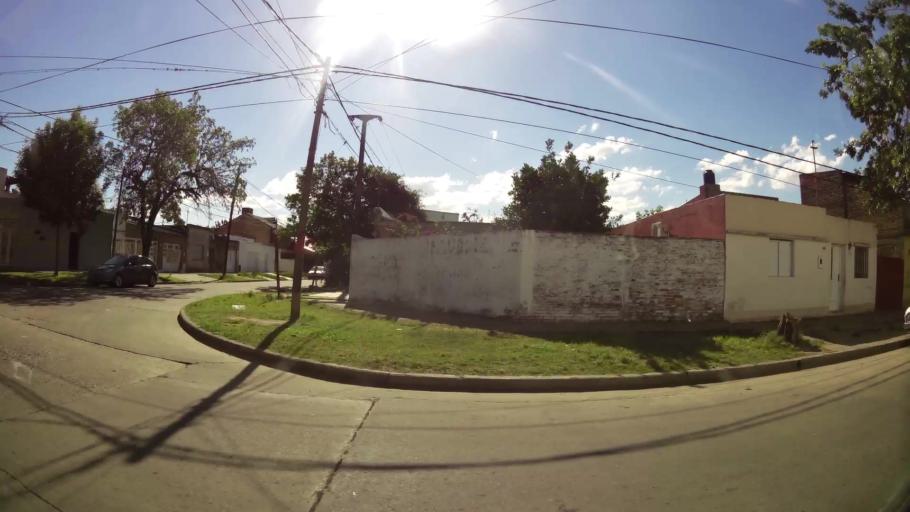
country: AR
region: Santa Fe
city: Santa Fe de la Vera Cruz
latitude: -31.6265
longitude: -60.6856
